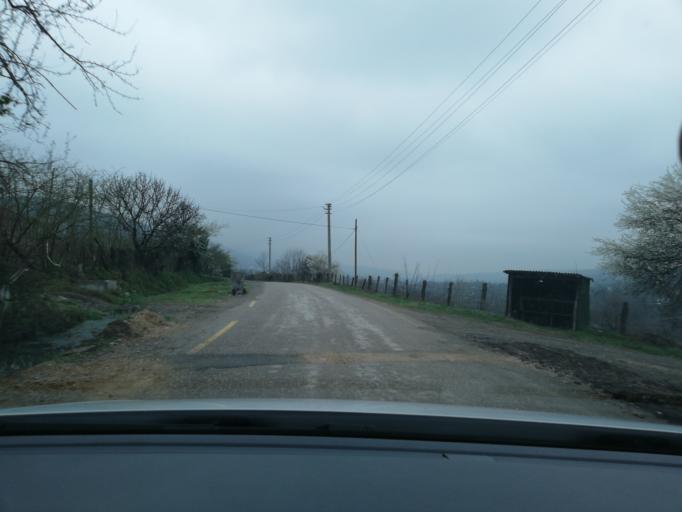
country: TR
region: Duzce
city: Kaynasli
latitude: 40.7748
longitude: 31.3501
